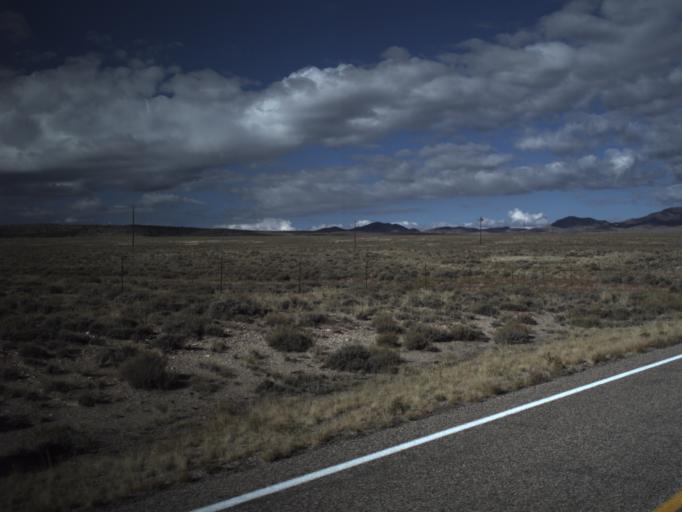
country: US
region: Utah
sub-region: Beaver County
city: Milford
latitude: 38.4258
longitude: -113.1174
